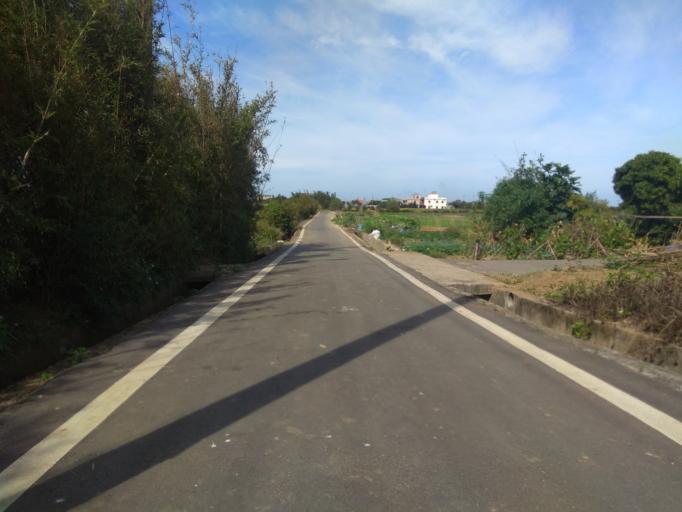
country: TW
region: Taiwan
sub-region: Hsinchu
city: Zhubei
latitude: 25.0138
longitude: 121.0771
